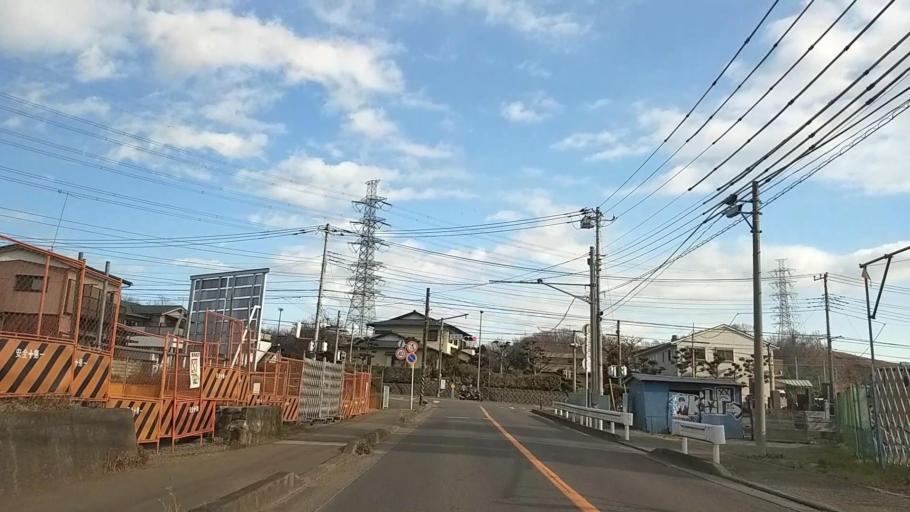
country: JP
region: Kanagawa
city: Isehara
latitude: 35.4155
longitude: 139.3022
